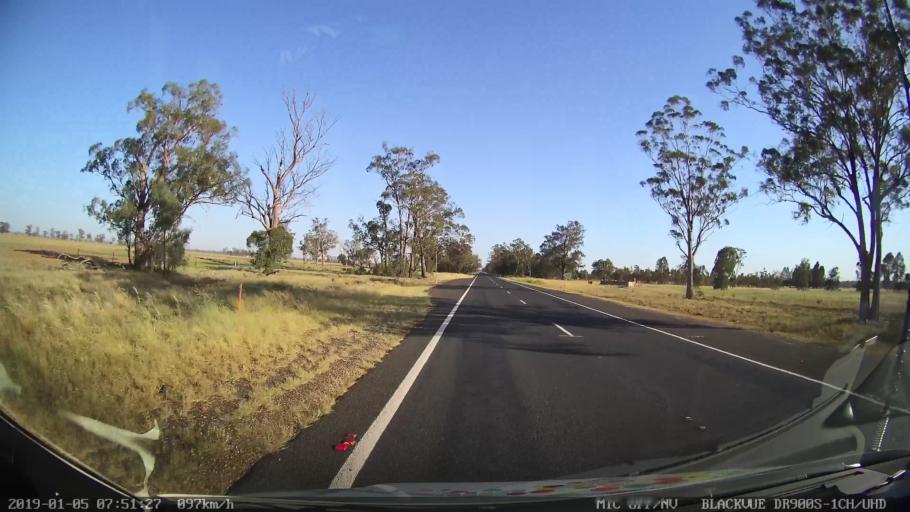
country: AU
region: New South Wales
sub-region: Gilgandra
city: Gilgandra
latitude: -31.7728
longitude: 148.6390
